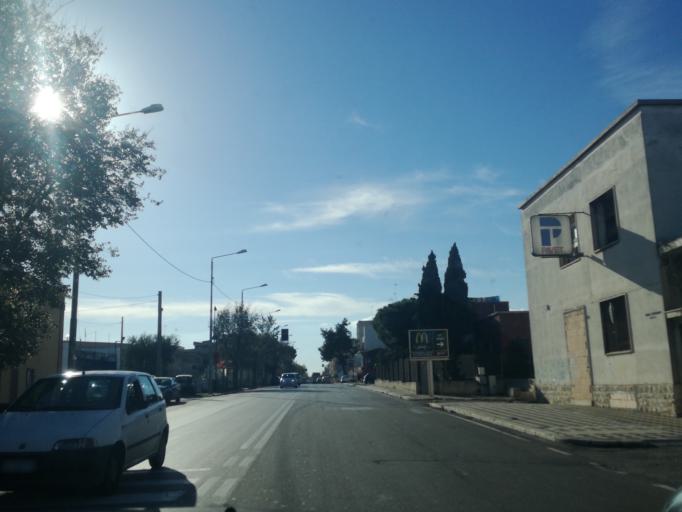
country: IT
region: Apulia
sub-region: Provincia di Bari
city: Bari
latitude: 41.1186
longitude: 16.8428
